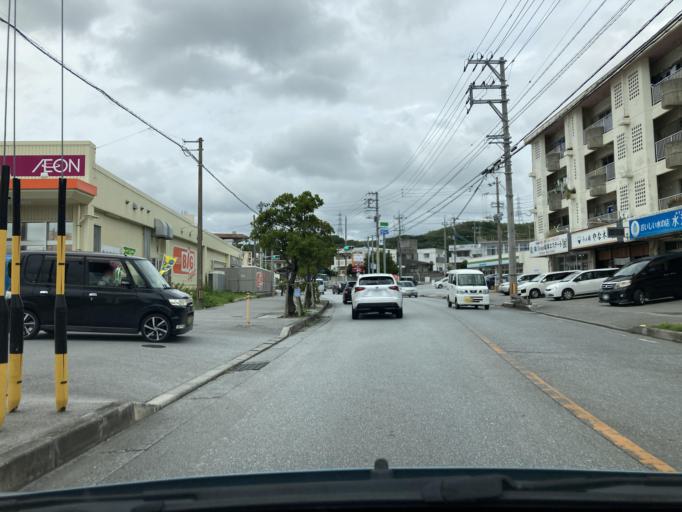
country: JP
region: Okinawa
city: Ginowan
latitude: 26.2268
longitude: 127.7627
